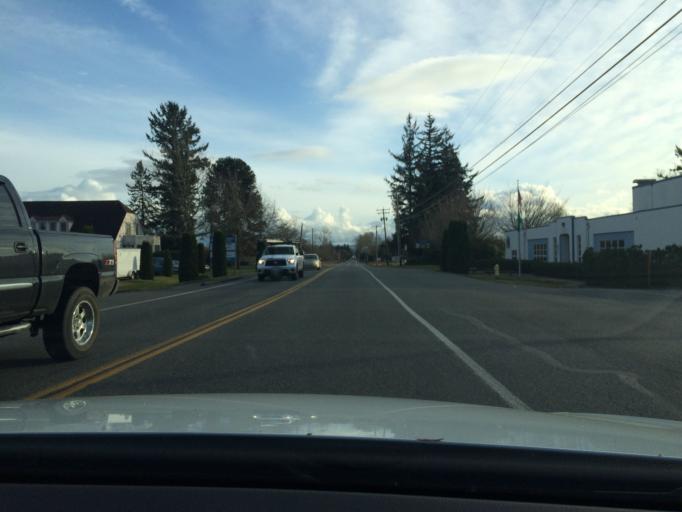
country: US
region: Washington
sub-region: Whatcom County
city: Marietta-Alderwood
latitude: 48.8332
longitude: -122.5408
